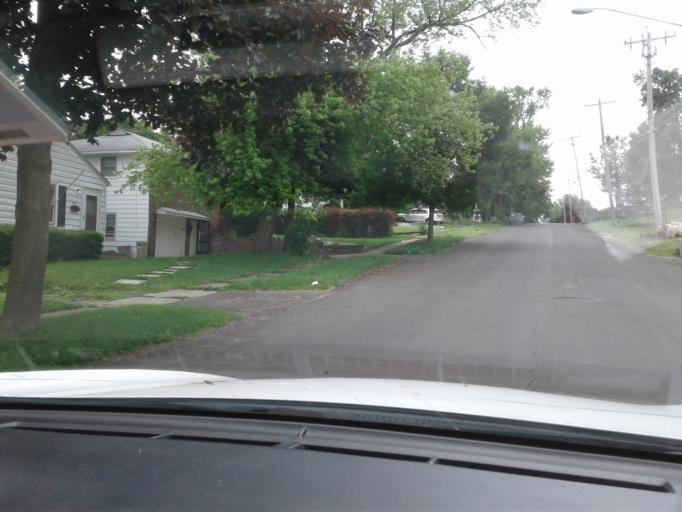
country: US
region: New York
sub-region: Onondaga County
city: East Syracuse
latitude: 43.0680
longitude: -76.0932
